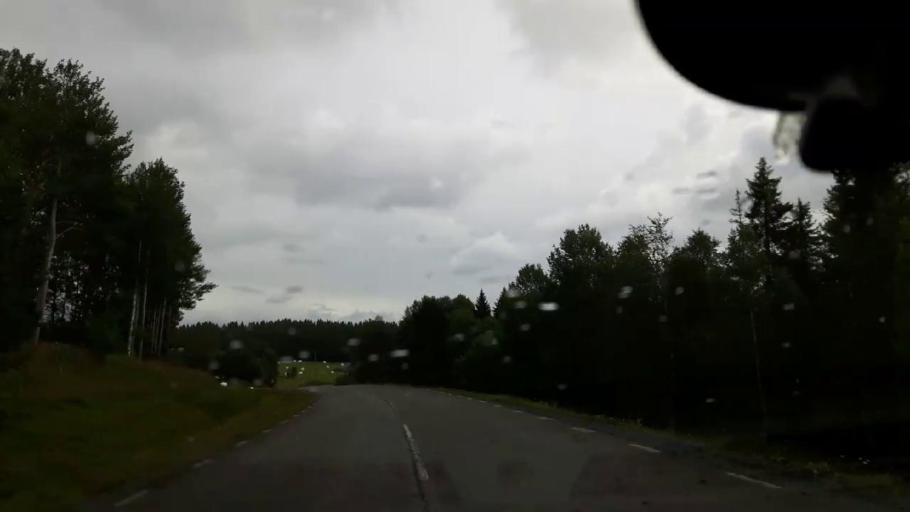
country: SE
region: Jaemtland
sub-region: Krokoms Kommun
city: Valla
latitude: 63.4120
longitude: 13.8077
